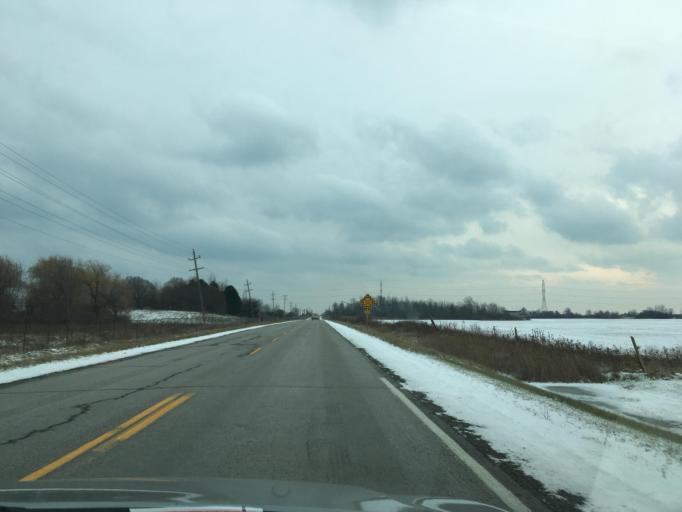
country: CA
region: Ontario
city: Norfolk County
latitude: 42.8109
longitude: -80.0628
